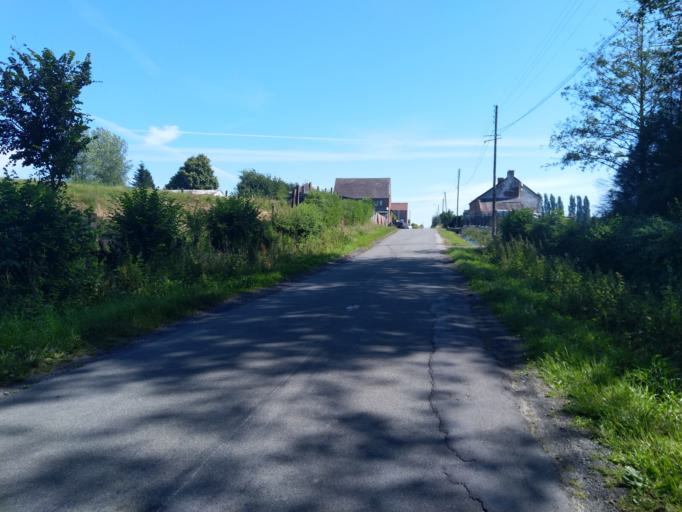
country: FR
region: Nord-Pas-de-Calais
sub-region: Departement du Nord
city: La Longueville
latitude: 50.3313
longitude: 3.8351
